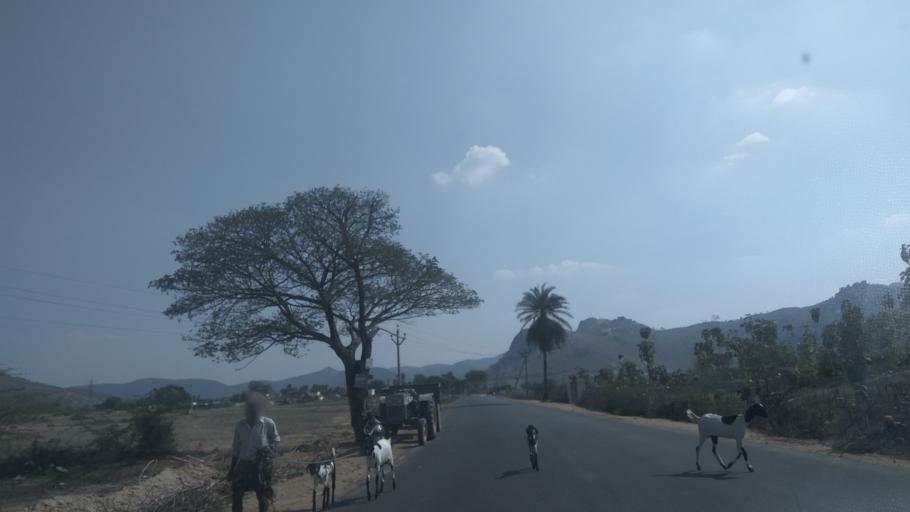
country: IN
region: Andhra Pradesh
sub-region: Chittoor
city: Renigunta
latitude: 13.5438
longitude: 79.4822
